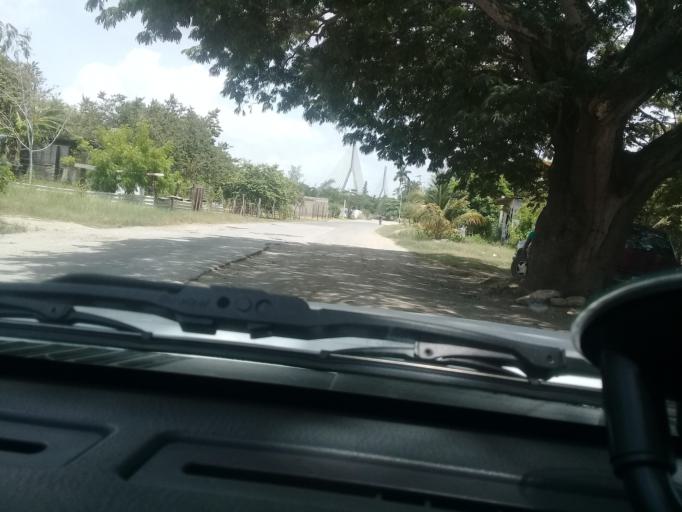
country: MX
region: Veracruz
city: Anahuac
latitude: 22.2242
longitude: -97.8287
